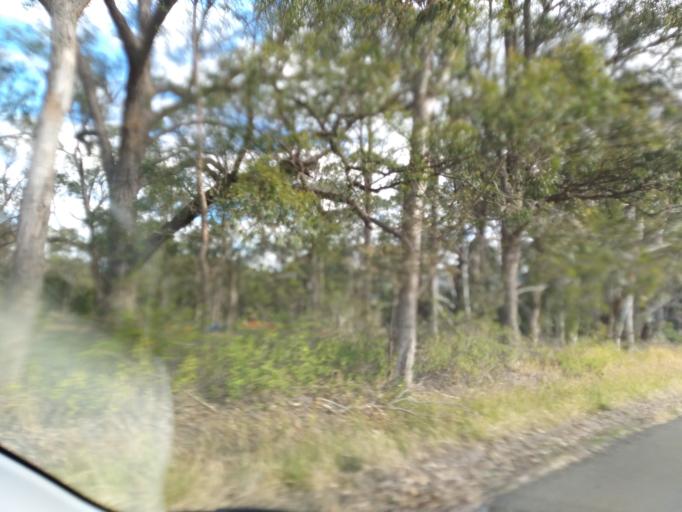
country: AU
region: New South Wales
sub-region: Shellharbour
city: Albion Park Rail
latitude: -34.5367
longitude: 150.7704
